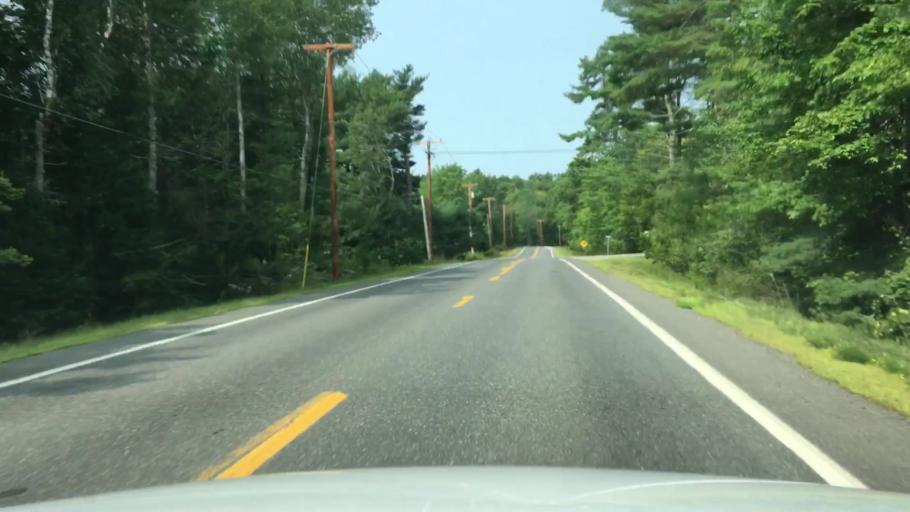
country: US
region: Maine
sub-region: Kennebec County
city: Chelsea
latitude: 44.3143
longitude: -69.7141
